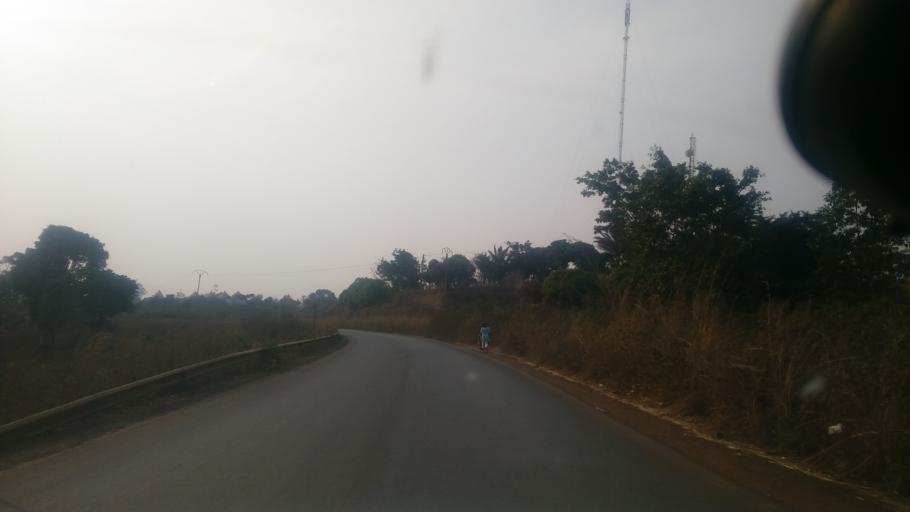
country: CM
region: West
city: Bangangte
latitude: 5.1624
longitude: 10.5050
